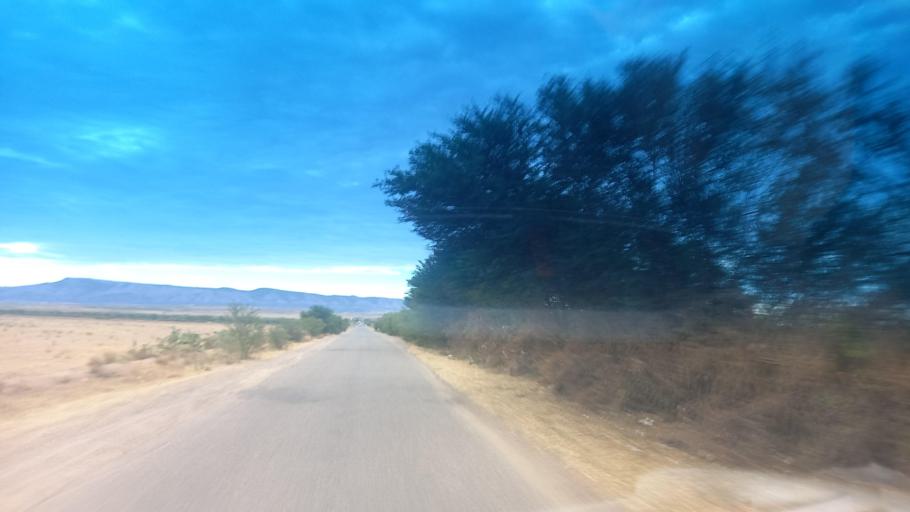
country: TN
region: Al Qasrayn
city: Sbiba
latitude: 35.3716
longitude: 9.0734
